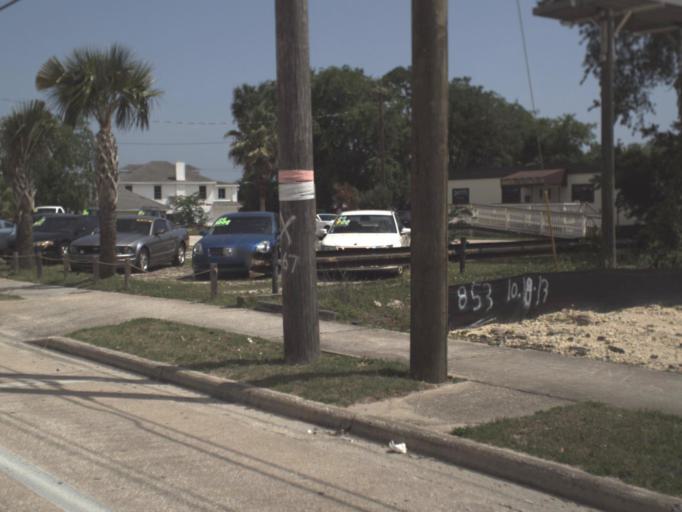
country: US
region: Florida
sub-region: Saint Johns County
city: Saint Augustine
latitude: 29.8889
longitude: -81.3243
